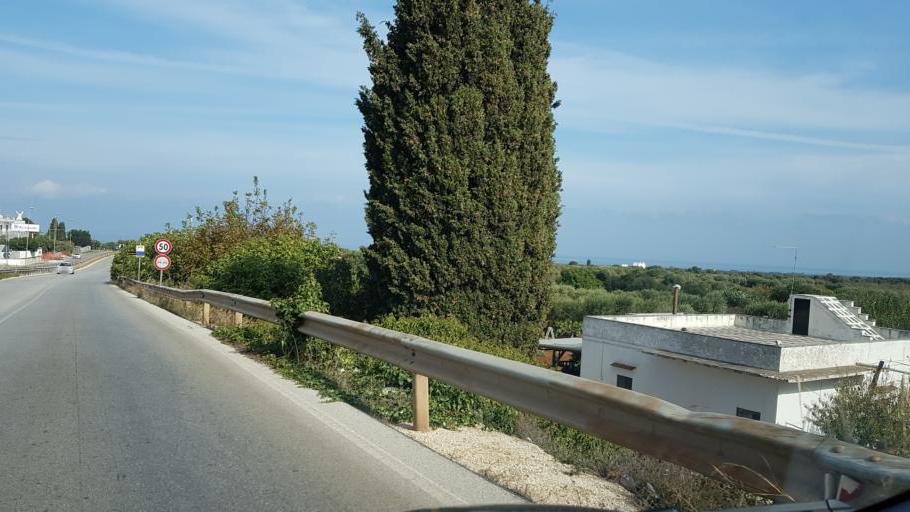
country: IT
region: Apulia
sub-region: Provincia di Brindisi
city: Ostuni
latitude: 40.7528
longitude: 17.5829
